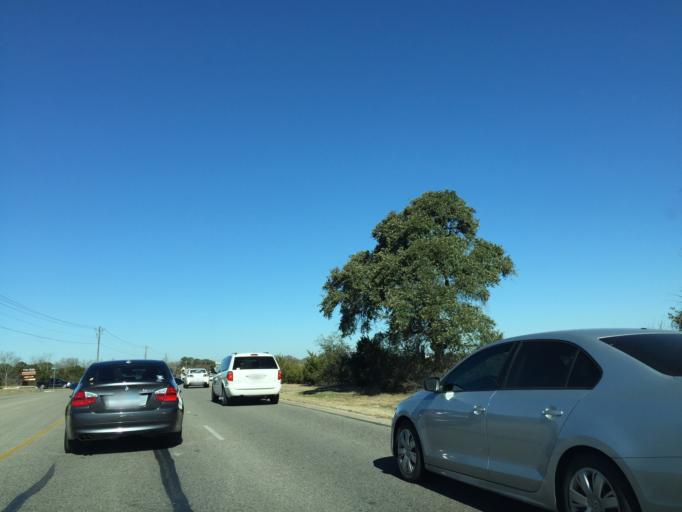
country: US
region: Texas
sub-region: Williamson County
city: Leander
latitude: 30.5697
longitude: -97.8688
